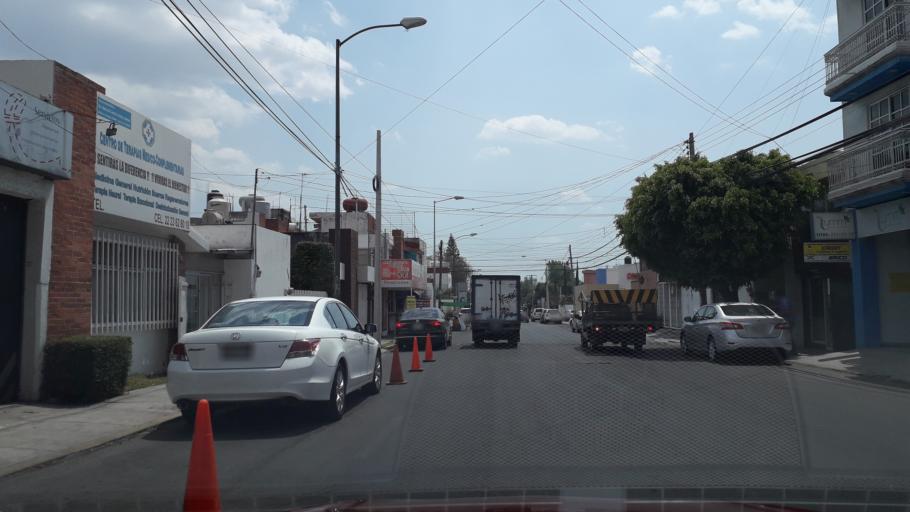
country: MX
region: Puebla
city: Puebla
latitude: 19.0334
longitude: -98.2222
